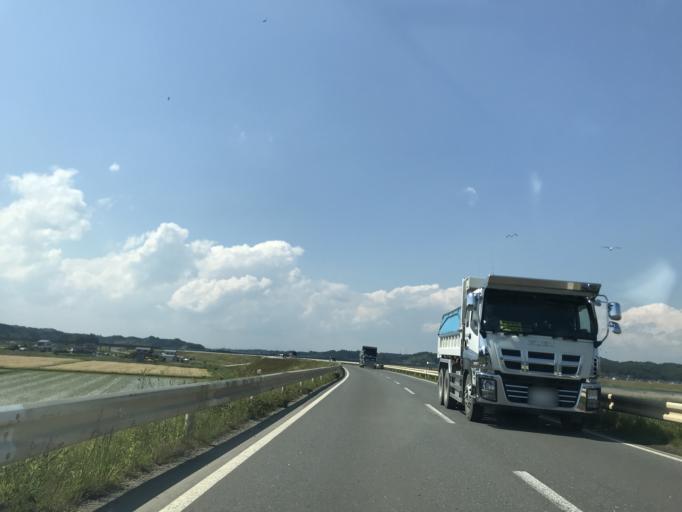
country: JP
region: Miyagi
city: Yamoto
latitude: 38.3825
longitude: 141.1682
